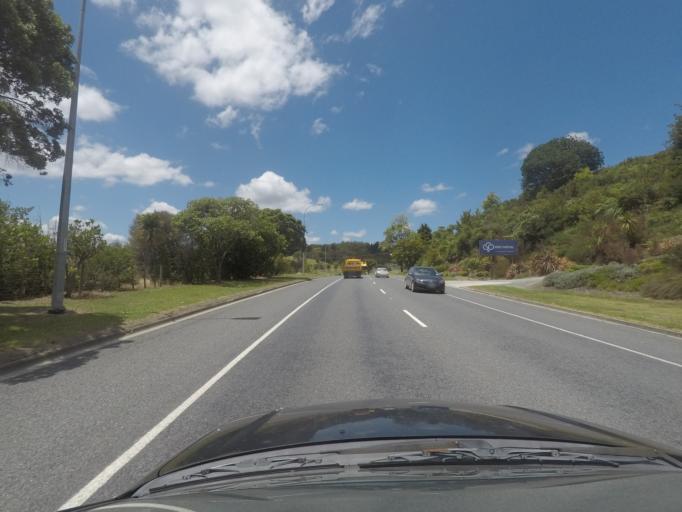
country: NZ
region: Northland
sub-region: Whangarei
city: Whangarei
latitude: -35.7442
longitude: 174.3262
